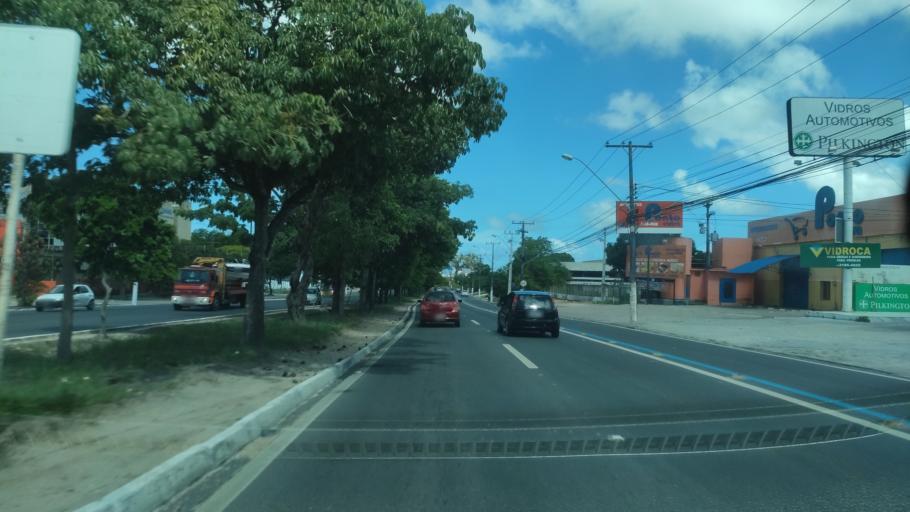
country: BR
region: Alagoas
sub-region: Maceio
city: Maceio
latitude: -9.6004
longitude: -35.7489
